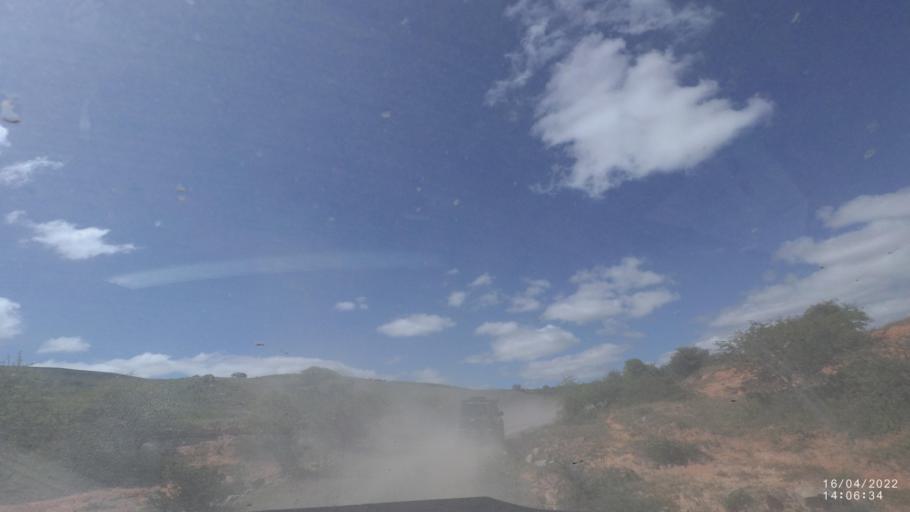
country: BO
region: Cochabamba
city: Mizque
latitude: -18.0579
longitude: -65.5311
